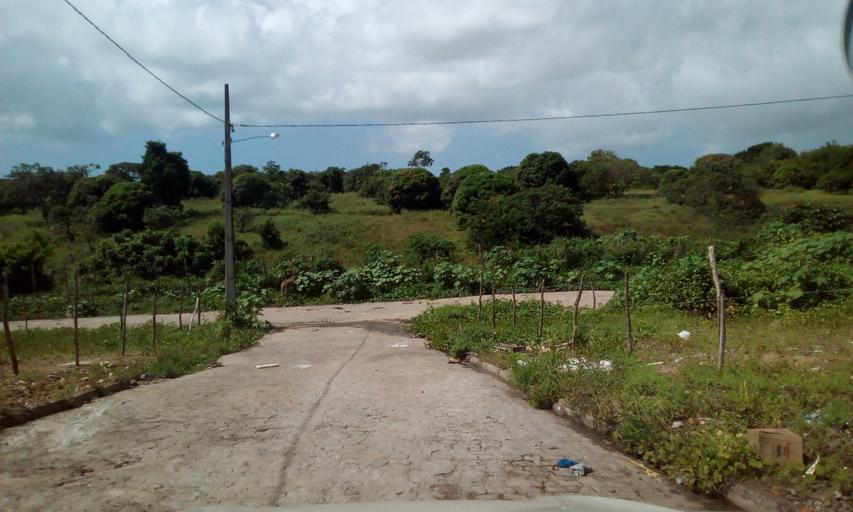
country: BR
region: Paraiba
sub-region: Conde
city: Conde
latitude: -7.2188
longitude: -34.8302
